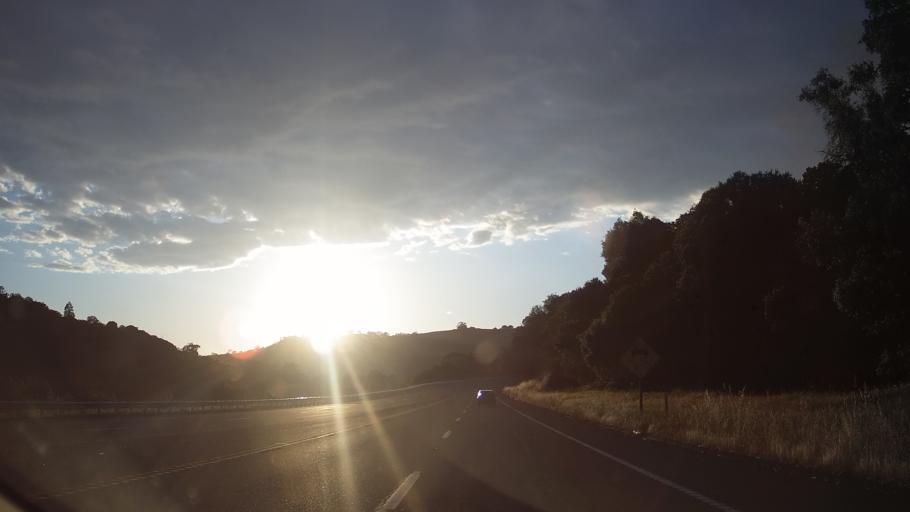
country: US
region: California
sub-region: Mendocino County
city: Redwood Valley
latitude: 39.2760
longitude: -123.2544
